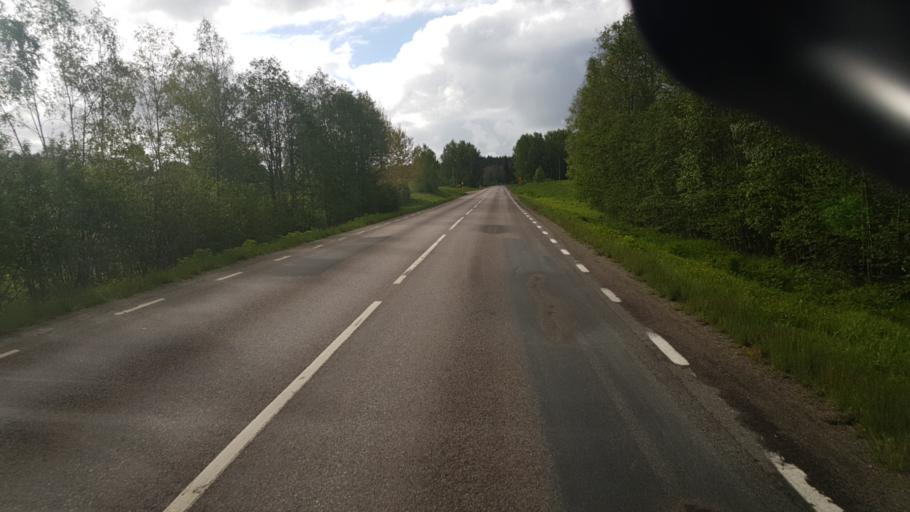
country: SE
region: Vaermland
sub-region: Eda Kommun
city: Amotfors
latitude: 59.6817
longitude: 12.3850
